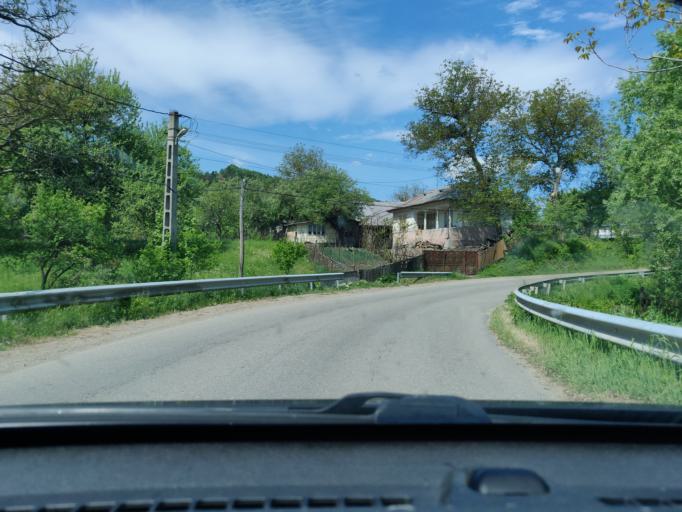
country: RO
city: Vizantea-Manastireasca
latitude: 45.9746
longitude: 26.8110
